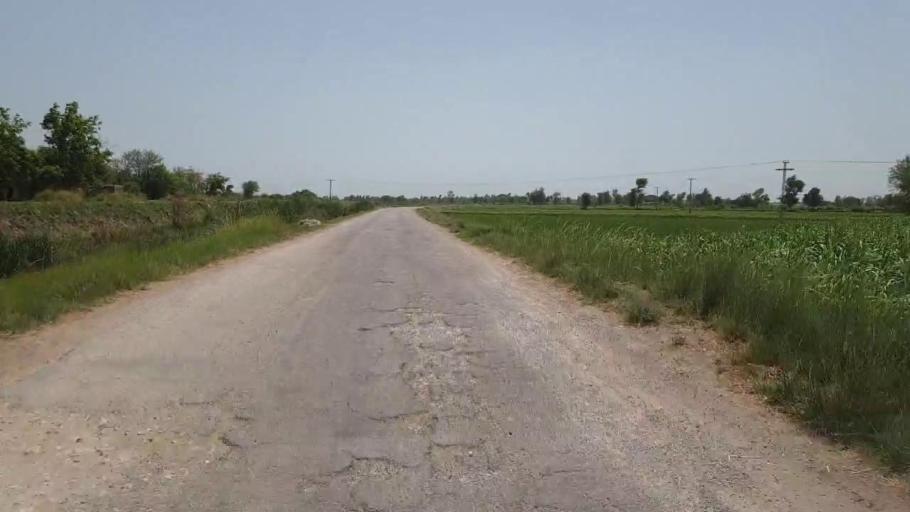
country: PK
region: Sindh
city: Daur
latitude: 26.3829
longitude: 68.1770
